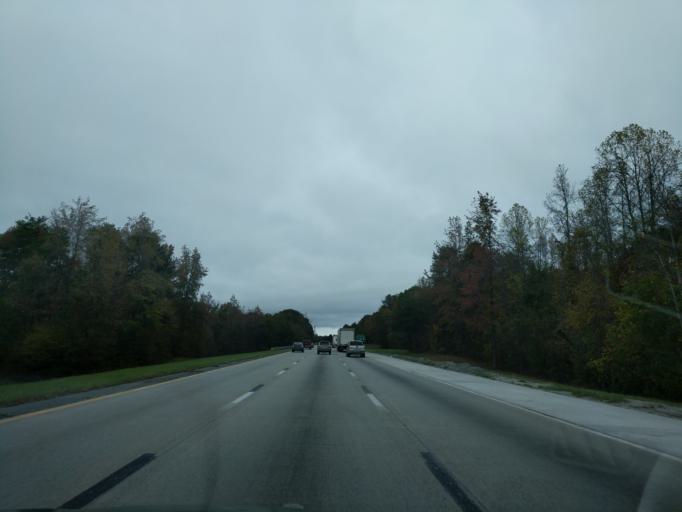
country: US
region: North Carolina
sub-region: Guilford County
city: Jamestown
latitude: 35.9716
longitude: -79.8909
